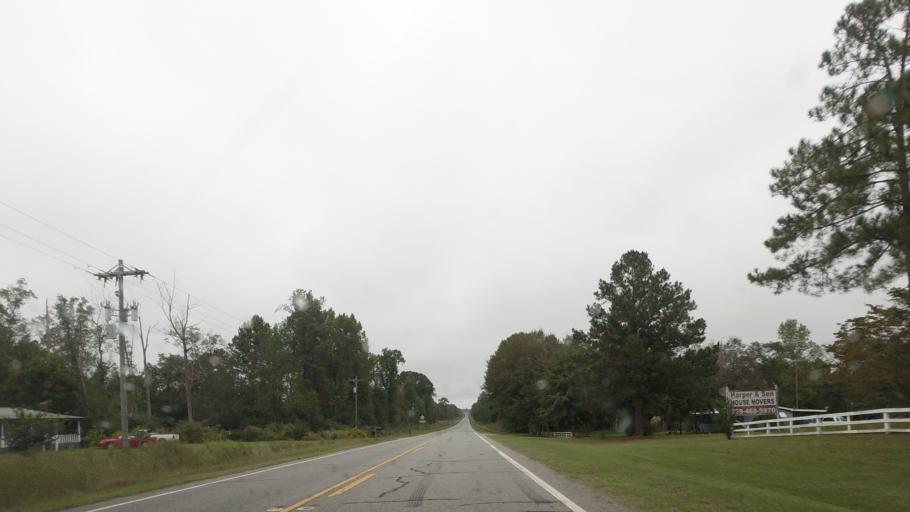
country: US
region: Georgia
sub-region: Irwin County
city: Ocilla
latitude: 31.4868
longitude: -83.2383
